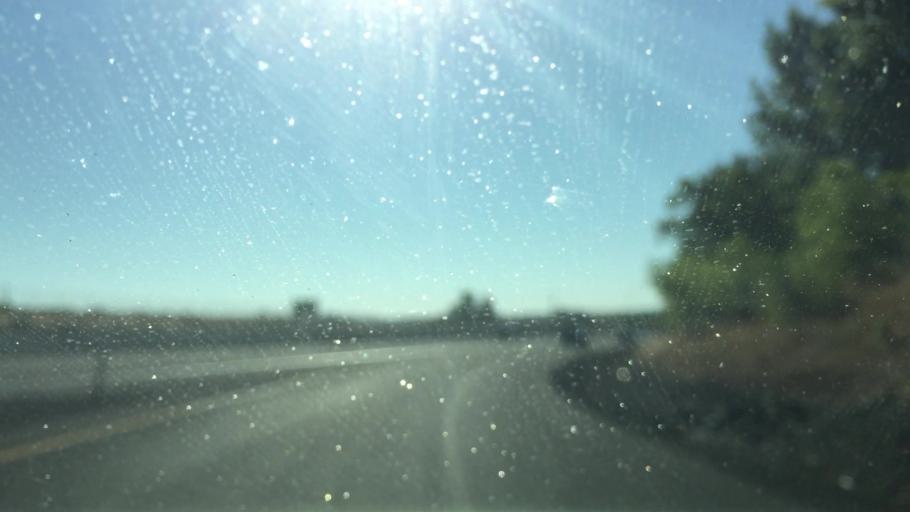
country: US
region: Washington
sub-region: Grant County
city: Moses Lake
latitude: 47.1427
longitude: -119.2756
